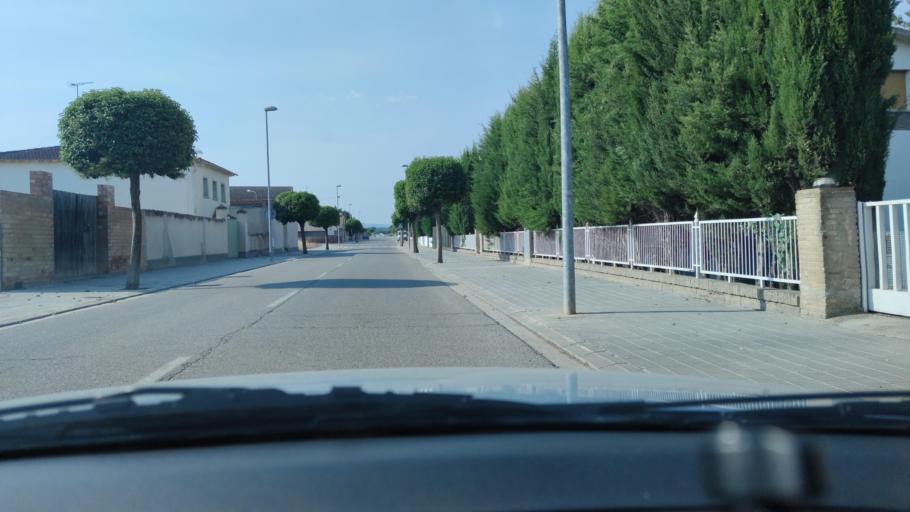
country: ES
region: Catalonia
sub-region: Provincia de Lleida
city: Juneda
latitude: 41.5779
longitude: 0.8324
